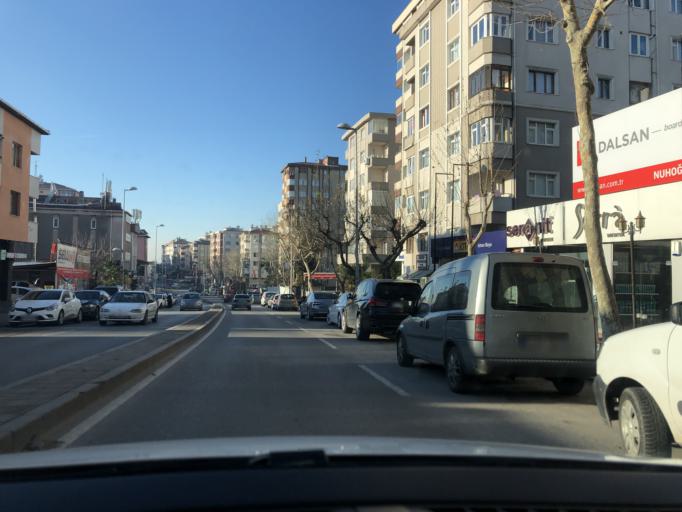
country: TR
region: Istanbul
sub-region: Atasehir
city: Atasehir
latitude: 40.9733
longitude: 29.1196
